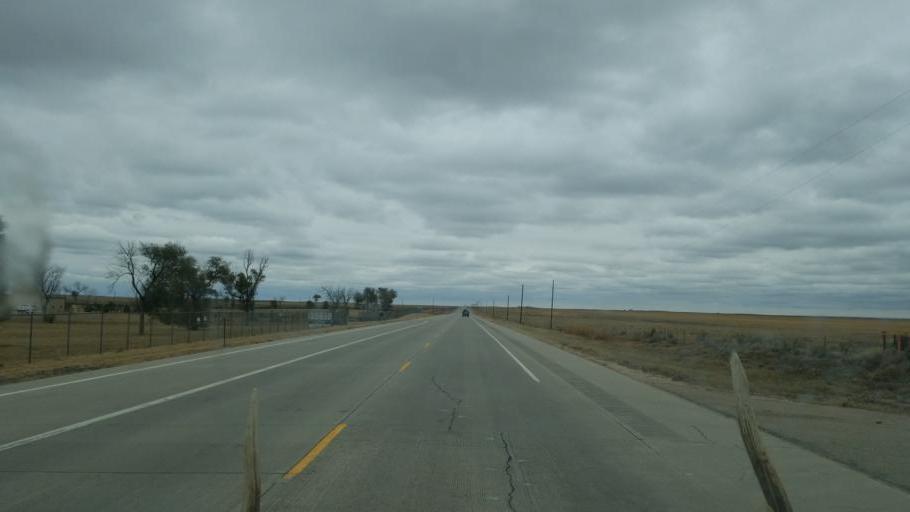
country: US
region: Colorado
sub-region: Kiowa County
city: Eads
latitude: 38.6579
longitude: -102.7858
